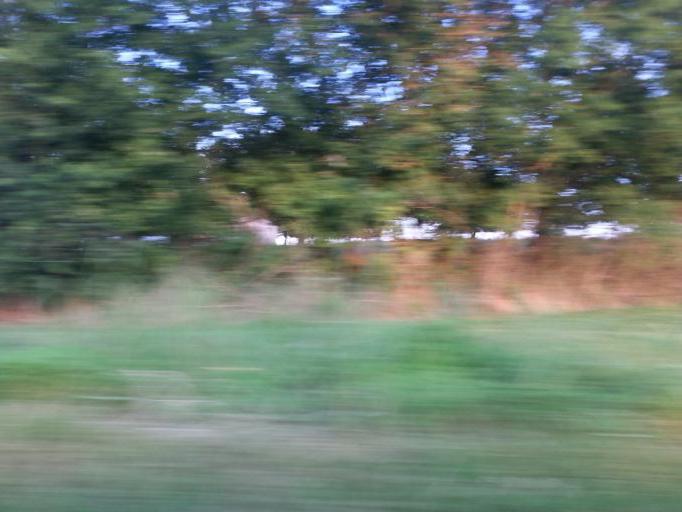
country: US
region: Tennessee
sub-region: Monroe County
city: Sweetwater
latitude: 35.6723
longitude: -84.4062
